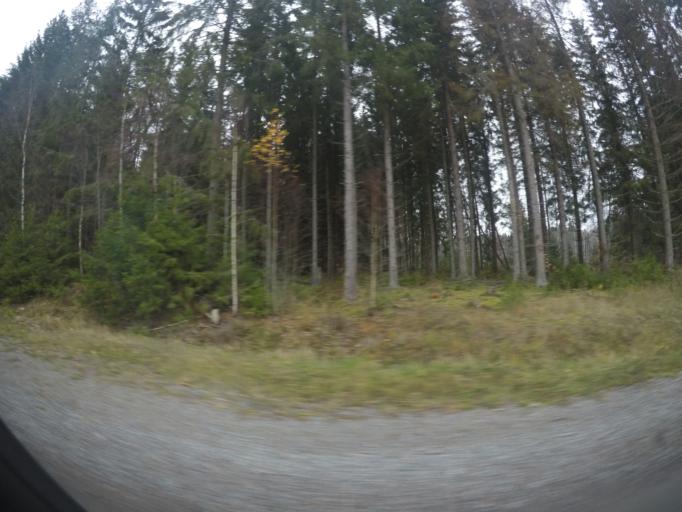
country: SE
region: Vaestmanland
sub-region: Surahammars Kommun
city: Ramnas
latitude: 59.7088
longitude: 16.0918
